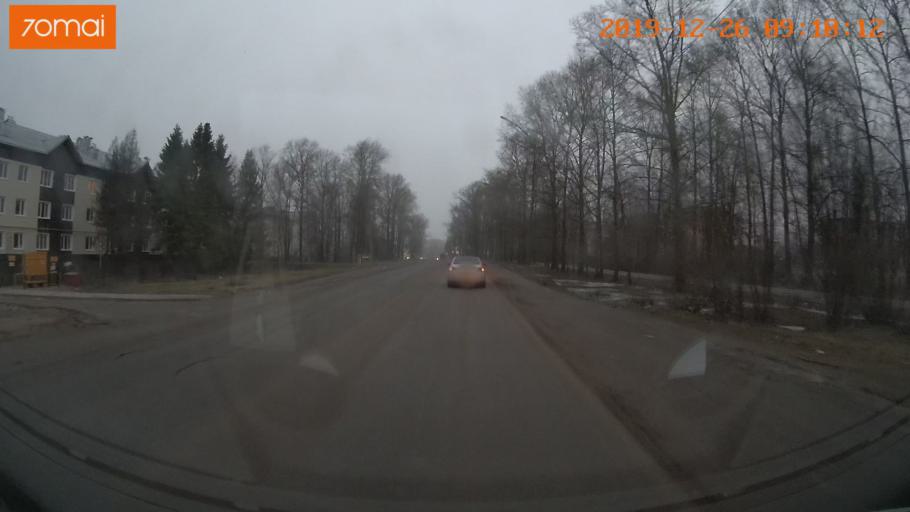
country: RU
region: Vologda
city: Gryazovets
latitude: 58.8696
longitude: 40.2528
